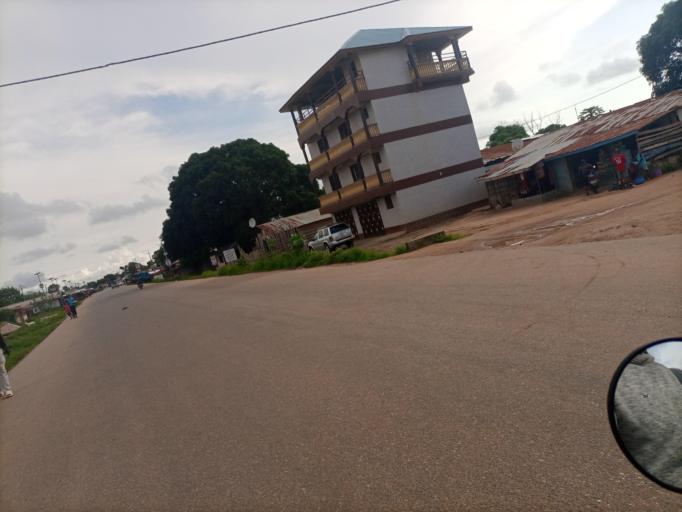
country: SL
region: Northern Province
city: Masoyila
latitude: 8.6075
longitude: -13.1781
